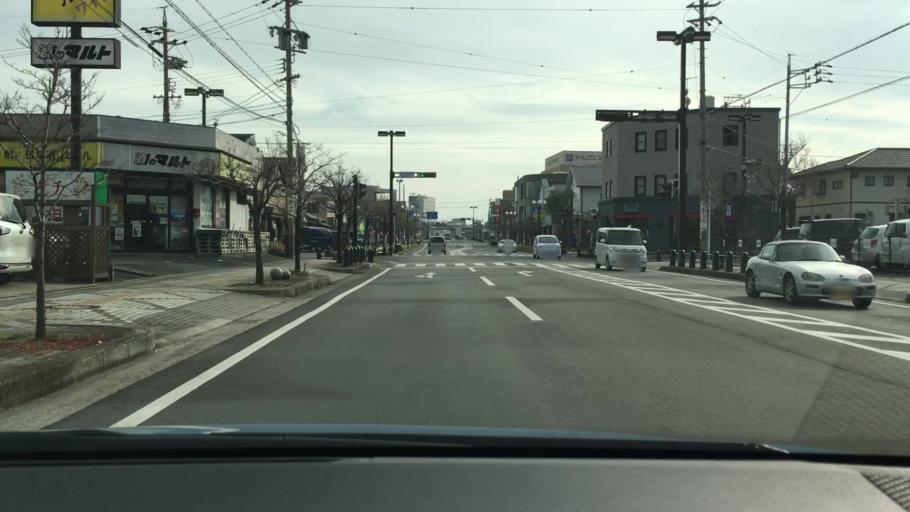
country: JP
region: Aichi
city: Tahara
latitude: 34.6713
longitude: 137.2702
